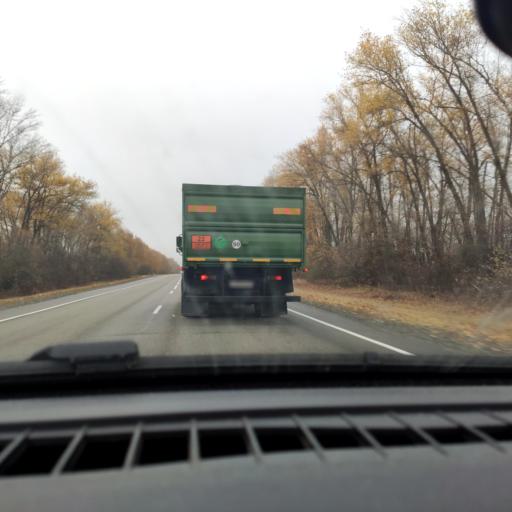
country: RU
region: Voronezj
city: Ostrogozhsk
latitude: 50.9912
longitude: 38.9980
